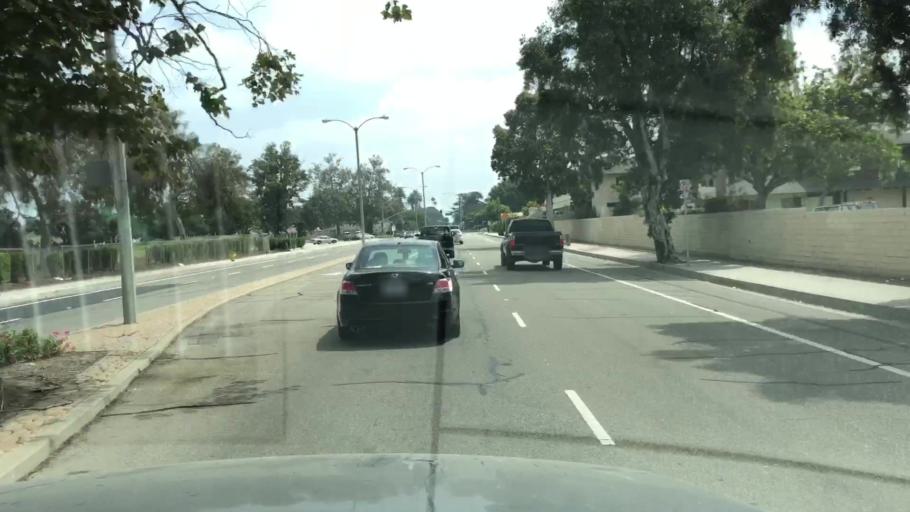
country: US
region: California
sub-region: Ventura County
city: Oxnard
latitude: 34.1977
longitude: -119.1904
